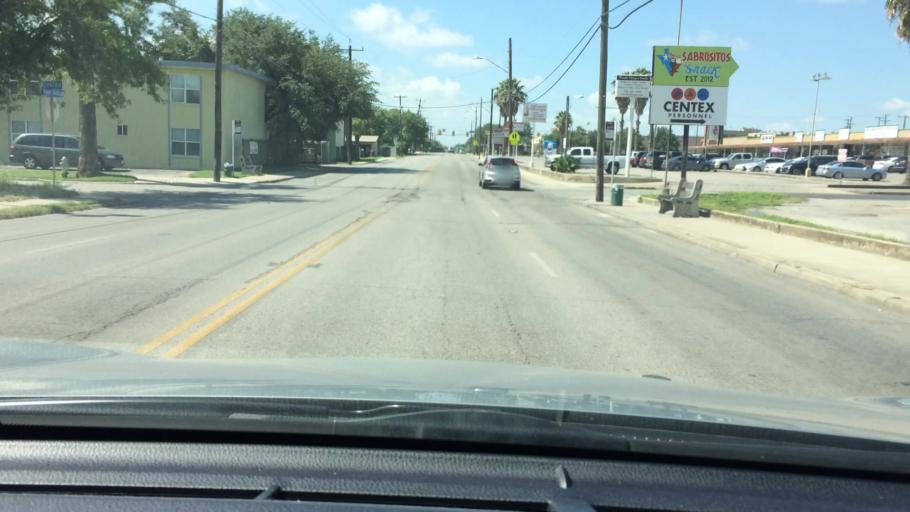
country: US
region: Texas
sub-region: Bexar County
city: Balcones Heights
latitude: 29.4927
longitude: -98.5351
